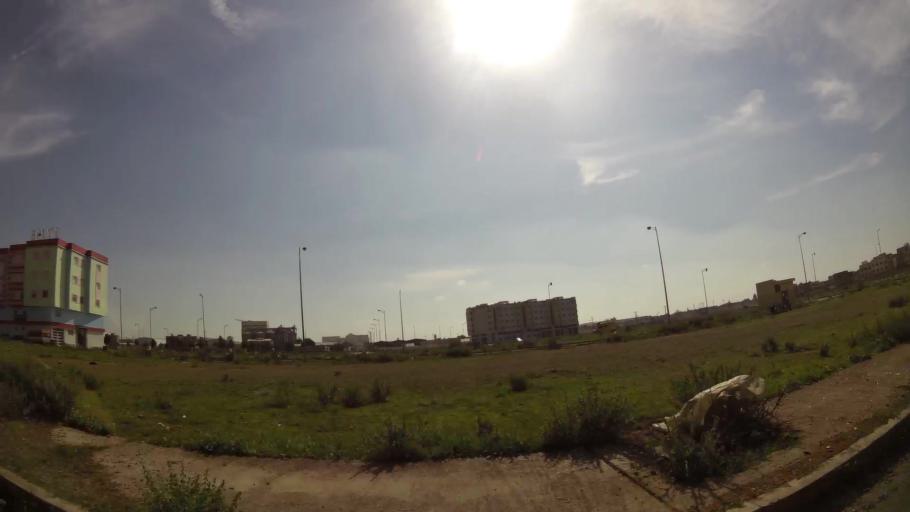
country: MA
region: Fes-Boulemane
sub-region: Fes
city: Fes
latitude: 34.0124
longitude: -5.0454
